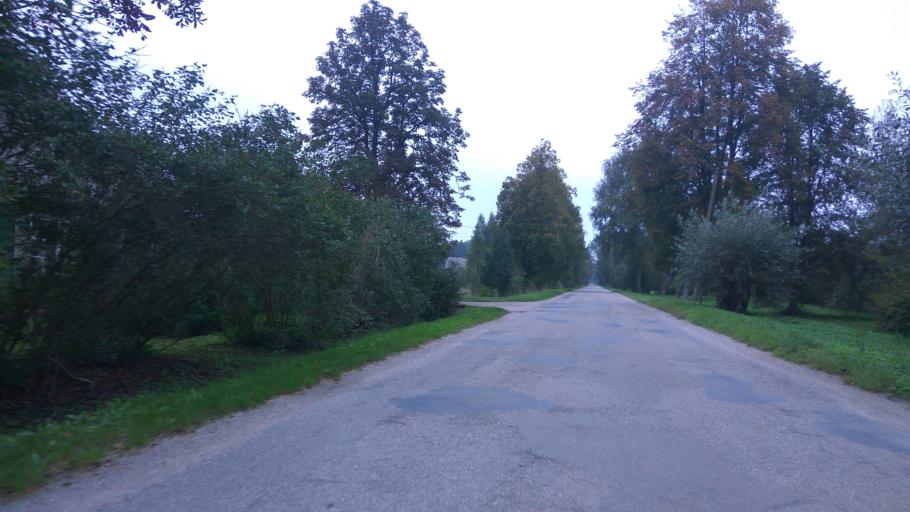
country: LV
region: Rucavas
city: Rucava
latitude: 56.1644
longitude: 21.1608
